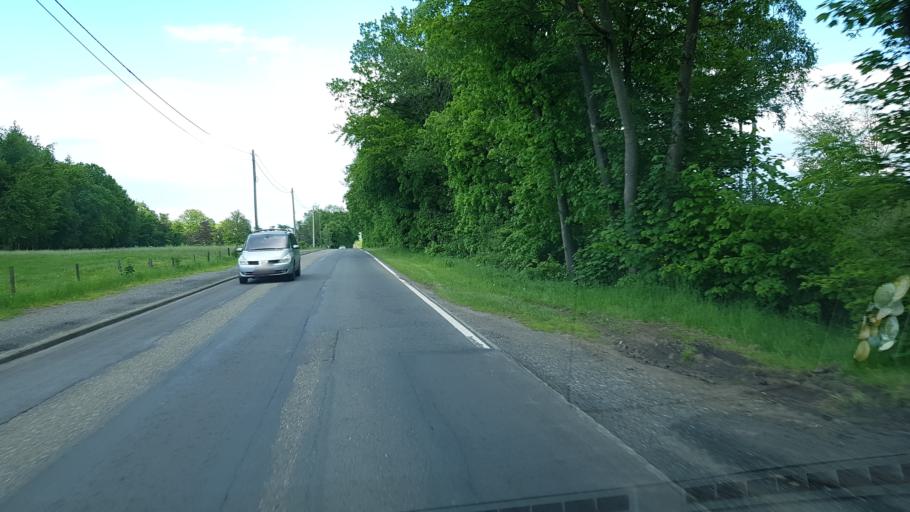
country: BE
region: Wallonia
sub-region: Province de Liege
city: Theux
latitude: 50.5451
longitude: 5.7743
